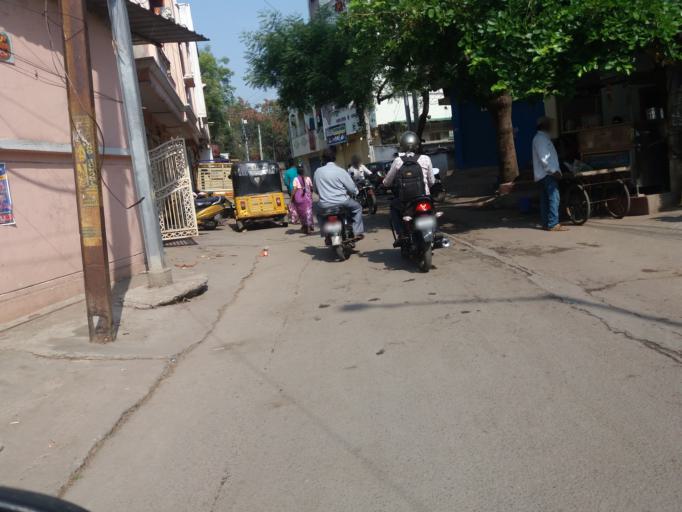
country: IN
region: Telangana
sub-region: Hyderabad
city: Malkajgiri
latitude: 17.4150
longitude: 78.5117
